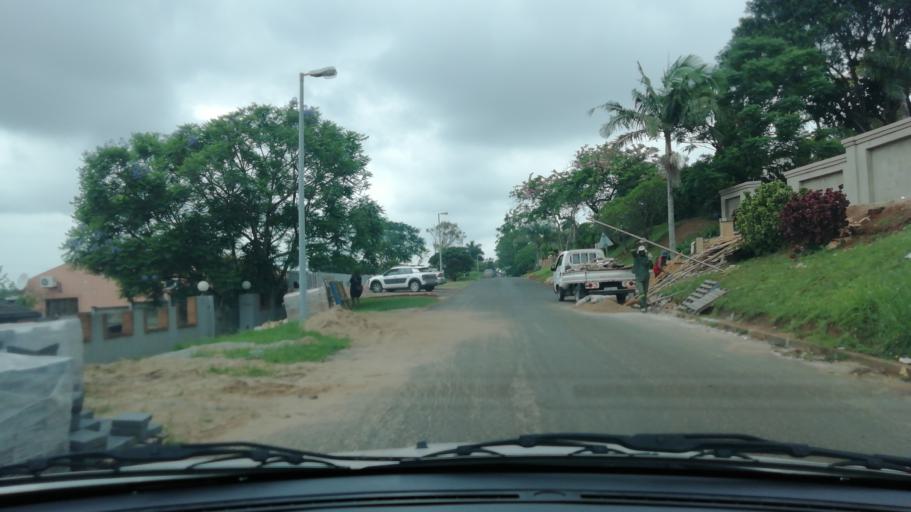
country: ZA
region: KwaZulu-Natal
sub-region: uThungulu District Municipality
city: Empangeni
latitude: -28.7671
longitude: 31.9020
